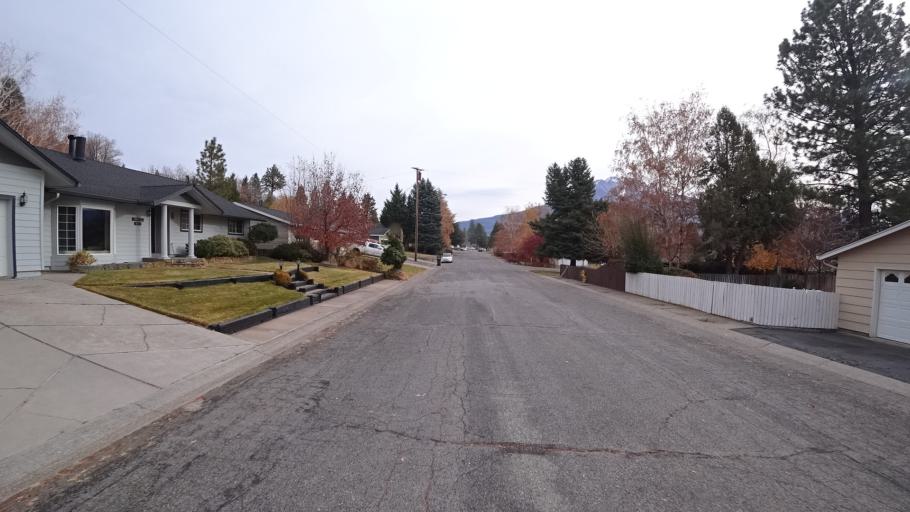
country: US
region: California
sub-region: Siskiyou County
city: Weed
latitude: 41.4171
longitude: -122.3907
